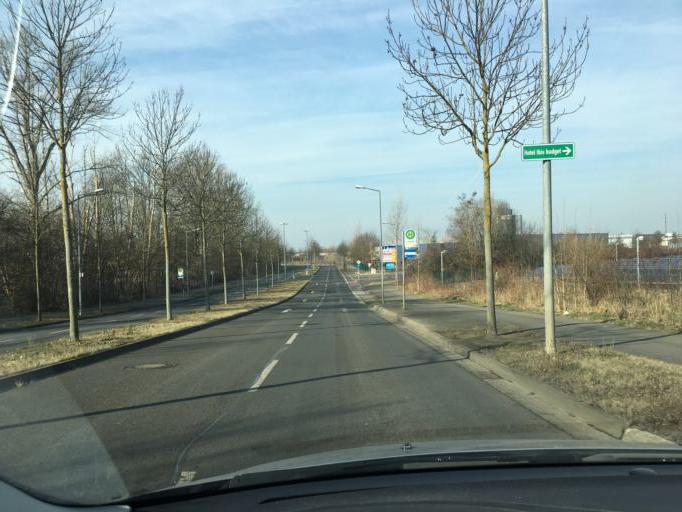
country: DE
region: Saxony
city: Taucha
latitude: 51.3615
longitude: 12.4397
